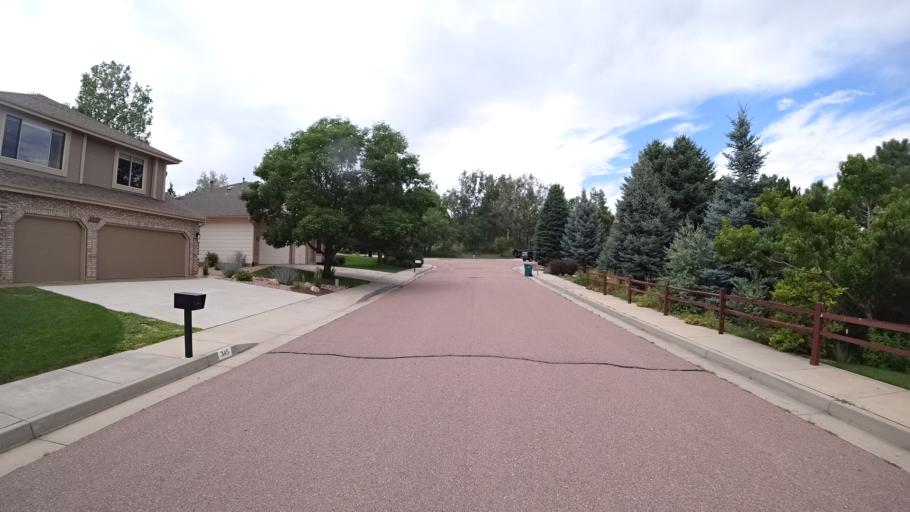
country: US
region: Colorado
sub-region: El Paso County
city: Colorado Springs
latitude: 38.9056
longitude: -104.8348
